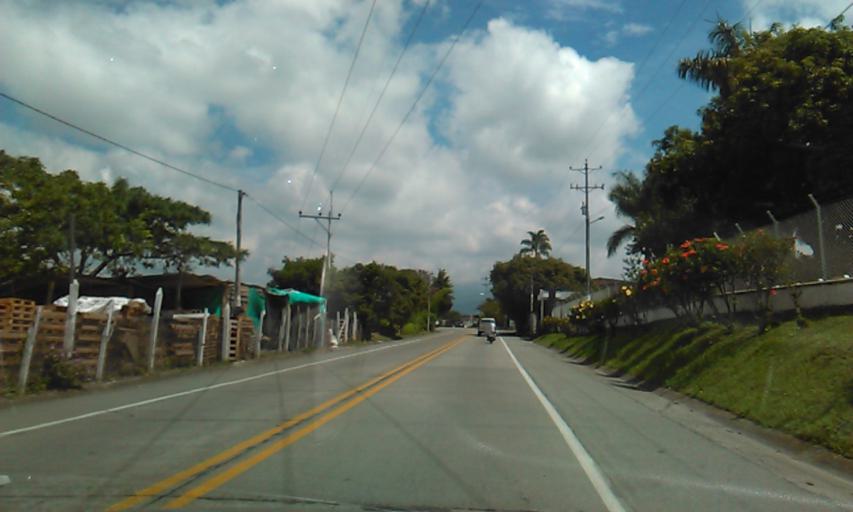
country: CO
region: Quindio
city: Armenia
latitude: 4.4965
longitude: -75.6944
